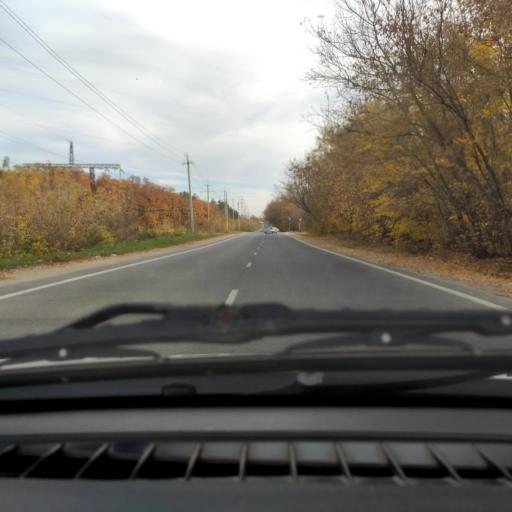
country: RU
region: Samara
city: Tol'yatti
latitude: 53.5077
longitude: 49.4540
